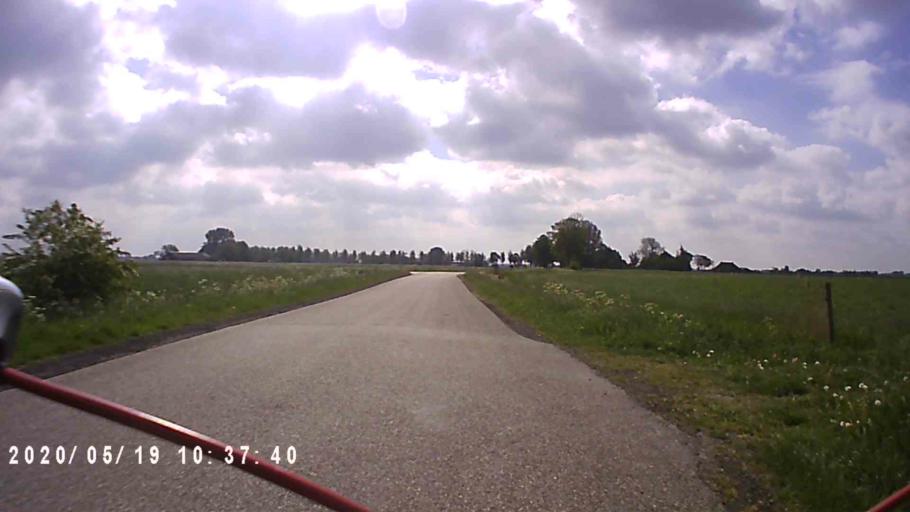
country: NL
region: Friesland
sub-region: Gemeente Kollumerland en Nieuwkruisland
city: Kollum
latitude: 53.2743
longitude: 6.1852
